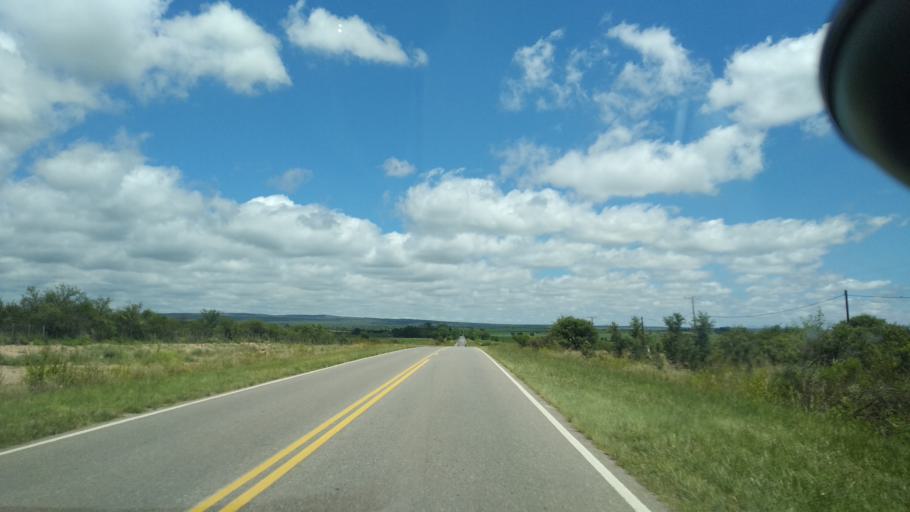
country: AR
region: Cordoba
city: Villa Cura Brochero
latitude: -31.6774
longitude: -65.0867
